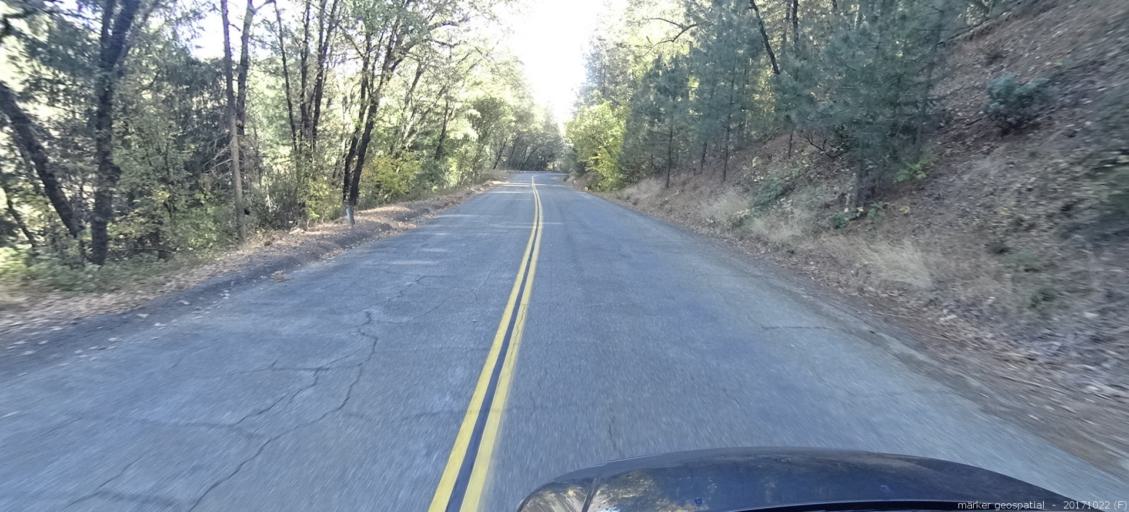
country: US
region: California
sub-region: Shasta County
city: Shasta Lake
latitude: 40.8582
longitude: -122.3533
